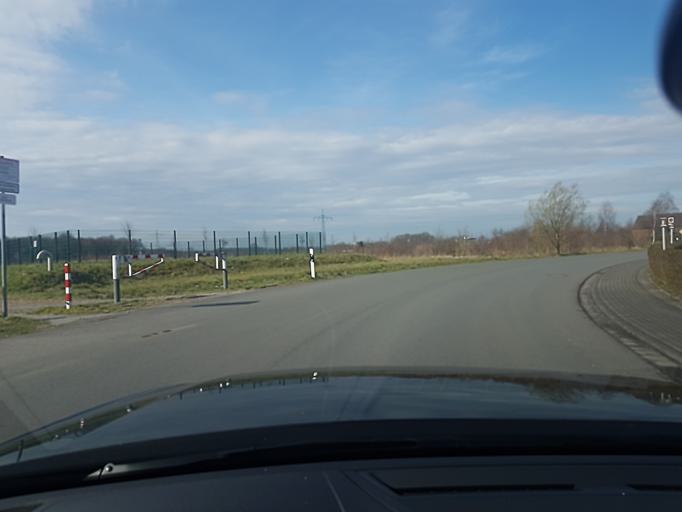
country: DE
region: North Rhine-Westphalia
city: Olfen
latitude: 51.7026
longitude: 7.4085
